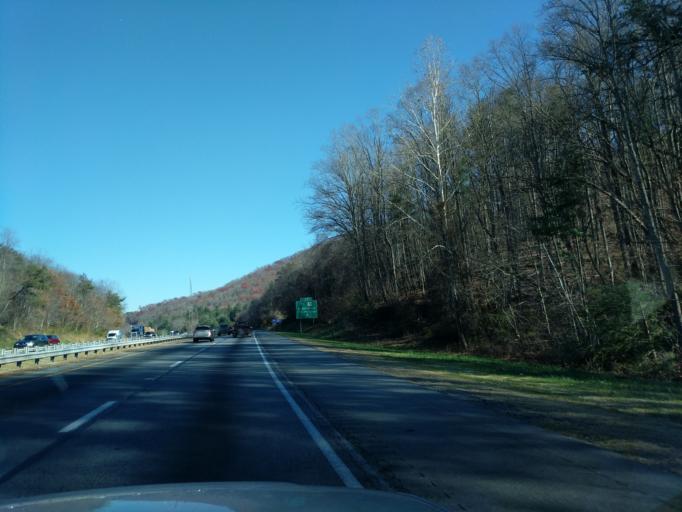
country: US
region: North Carolina
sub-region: Buncombe County
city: Swannanoa
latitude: 35.5788
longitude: -82.4701
